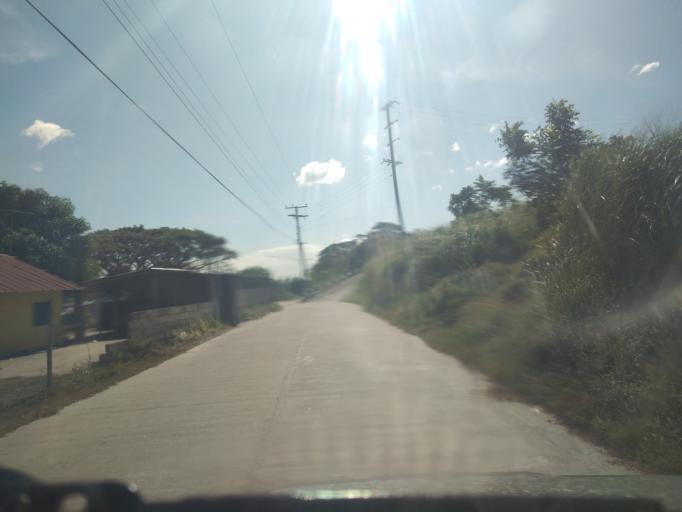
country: PH
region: Central Luzon
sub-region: Province of Pampanga
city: Calibutbut
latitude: 15.0889
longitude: 120.6000
